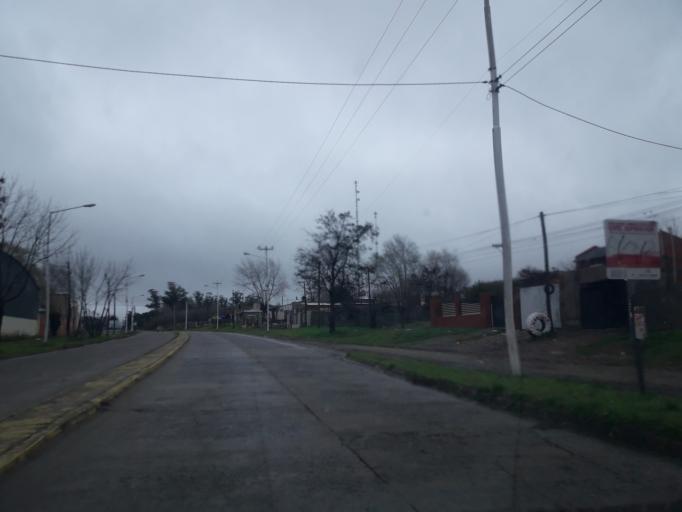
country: AR
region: Buenos Aires
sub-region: Partido de Tandil
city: Tandil
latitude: -37.3242
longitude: -59.1701
